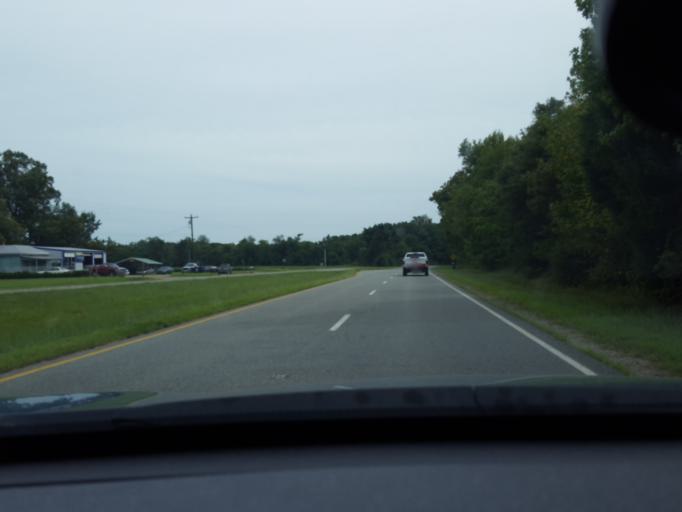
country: US
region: Virginia
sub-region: Caroline County
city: Bowling Green
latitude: 38.0108
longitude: -77.3349
